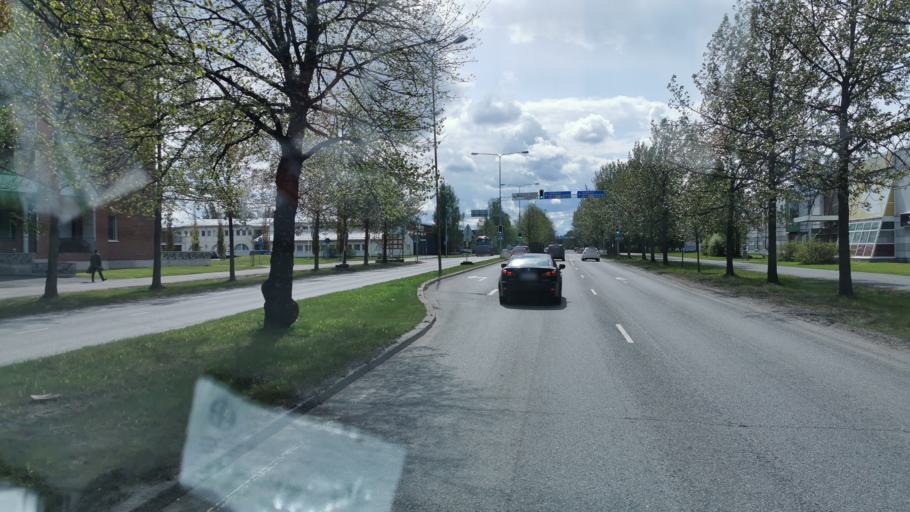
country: FI
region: Northern Ostrobothnia
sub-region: Oulu
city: Oulu
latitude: 64.9998
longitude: 25.4640
